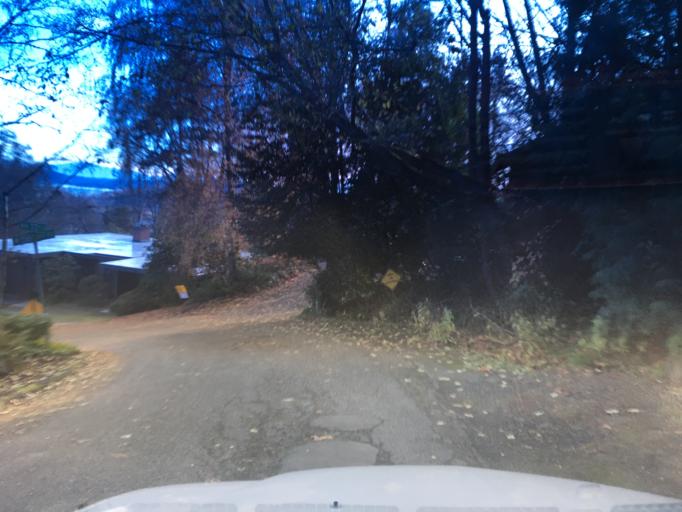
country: US
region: Washington
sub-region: King County
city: Inglewood-Finn Hill
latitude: 47.6847
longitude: -122.2674
